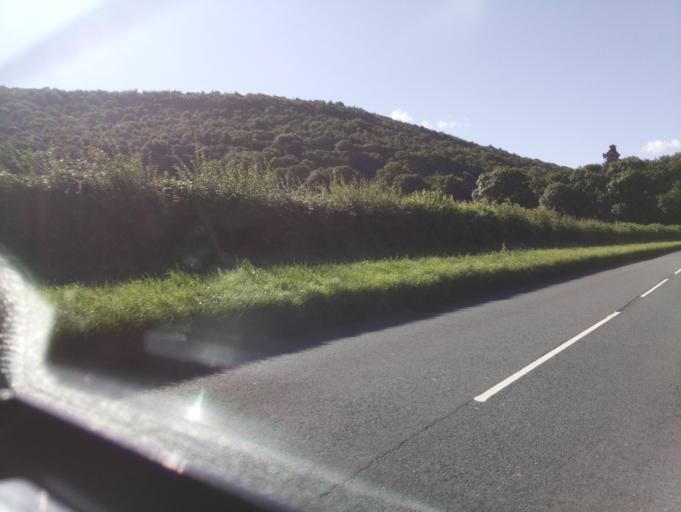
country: GB
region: England
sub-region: Herefordshire
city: Walford
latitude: 51.8987
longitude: -2.5898
